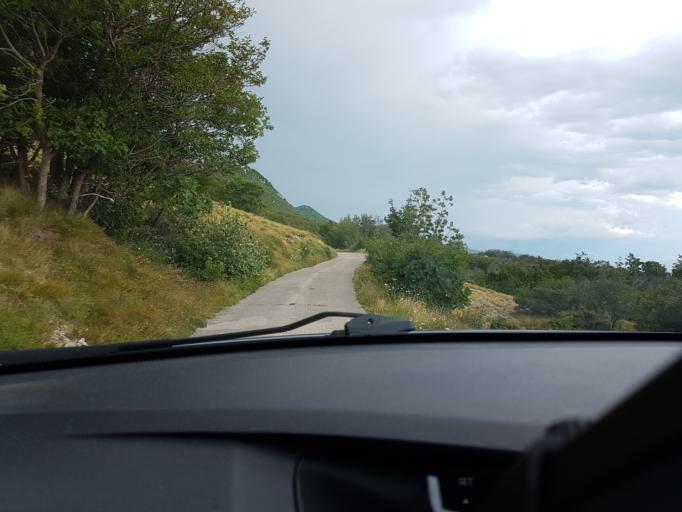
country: HR
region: Primorsko-Goranska
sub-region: Grad Crikvenica
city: Crikvenica
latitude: 45.2376
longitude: 14.6953
